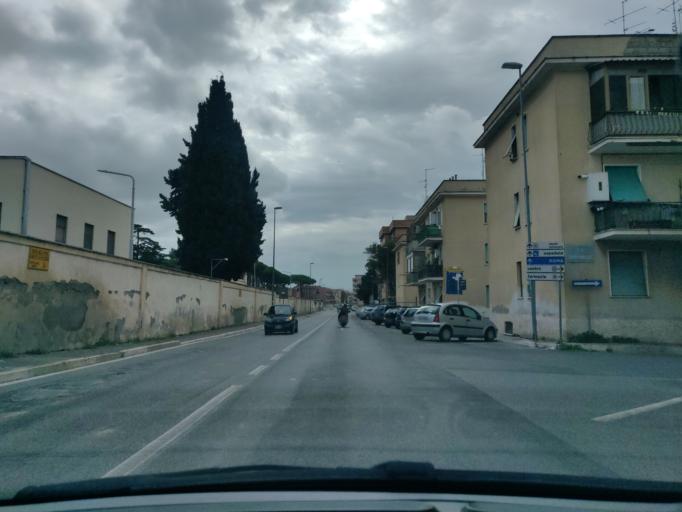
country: IT
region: Latium
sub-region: Citta metropolitana di Roma Capitale
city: Civitavecchia
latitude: 42.0986
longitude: 11.8004
